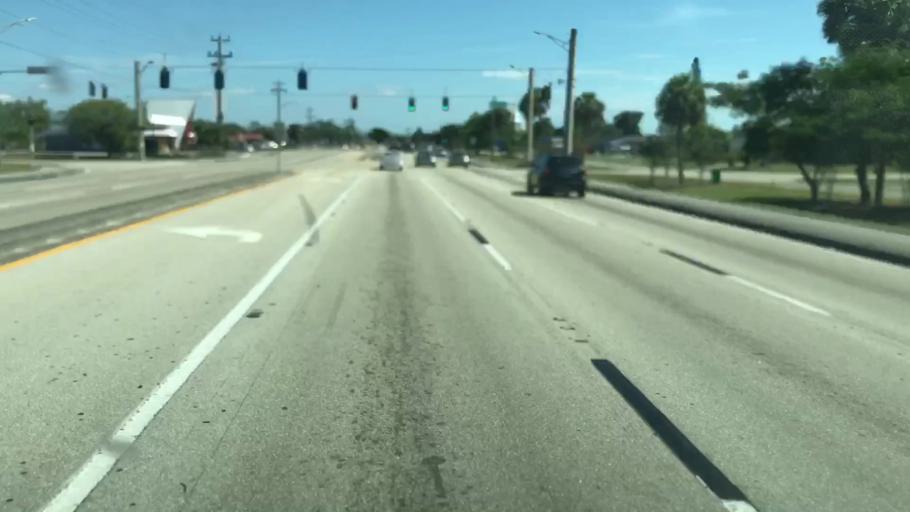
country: US
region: Florida
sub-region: Lee County
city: Lehigh Acres
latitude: 26.6142
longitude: -81.6591
